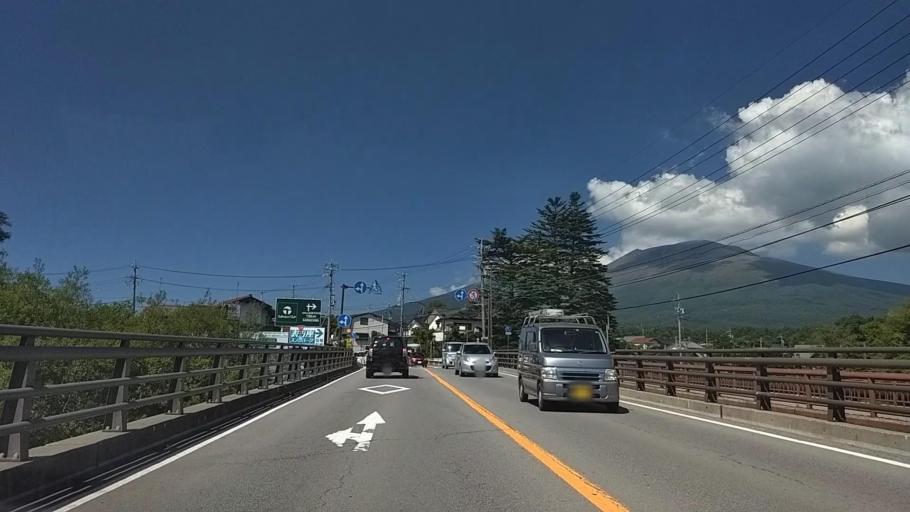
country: JP
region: Nagano
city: Komoro
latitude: 36.3486
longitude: 138.5956
